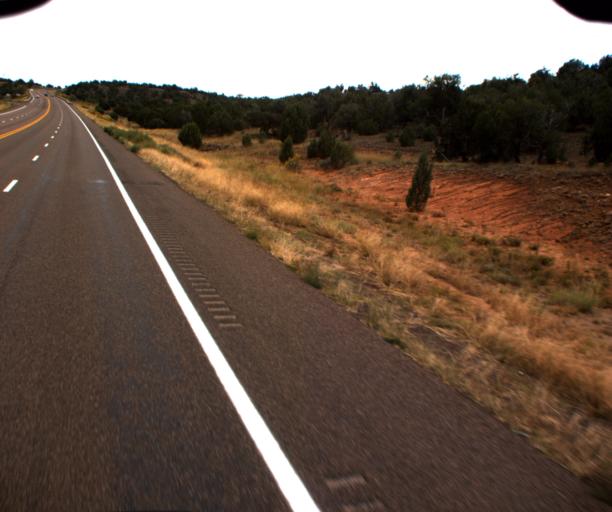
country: US
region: Arizona
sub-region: Navajo County
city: White Mountain Lake
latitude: 34.3800
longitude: -110.0573
